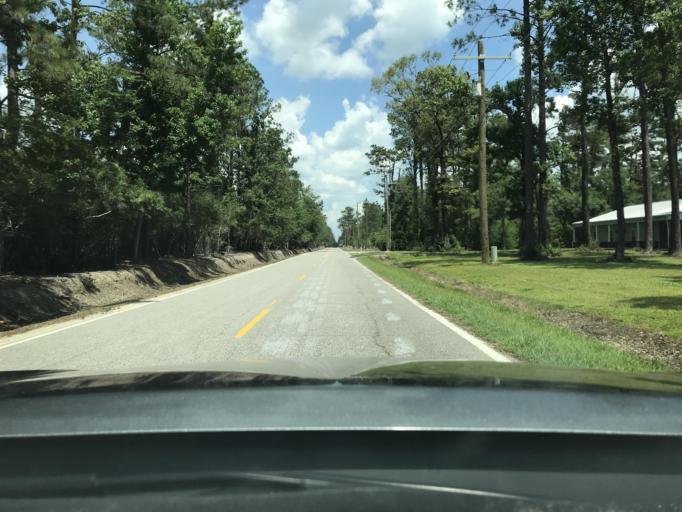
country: US
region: Louisiana
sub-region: Calcasieu Parish
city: Moss Bluff
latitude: 30.3300
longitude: -93.1536
